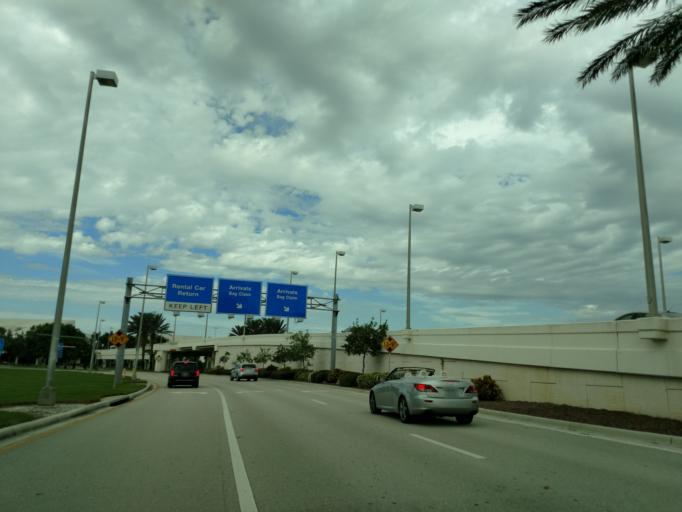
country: US
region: Florida
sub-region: Lee County
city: Gateway
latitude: 26.5253
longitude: -81.7525
